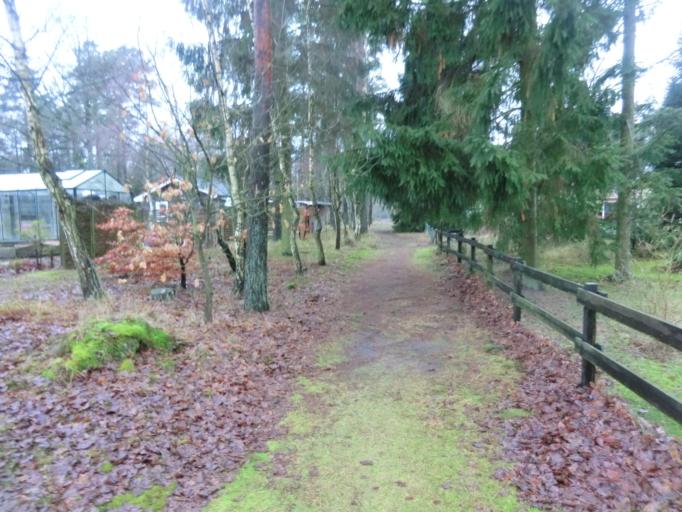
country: SE
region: Skane
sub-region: Hoors Kommun
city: Loberod
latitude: 55.7339
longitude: 13.4076
